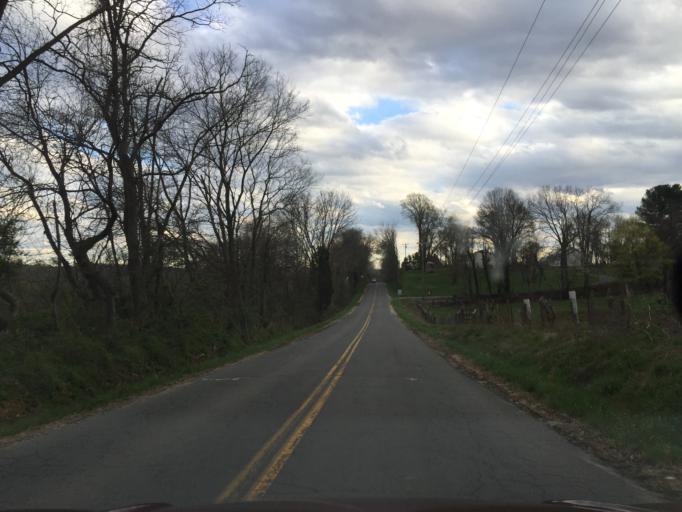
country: US
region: Maryland
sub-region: Frederick County
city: Point of Rocks
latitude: 39.2803
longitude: -77.5870
